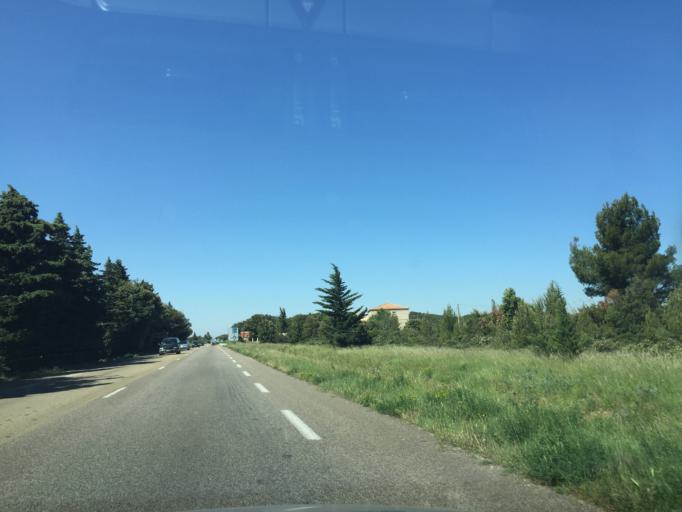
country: FR
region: Languedoc-Roussillon
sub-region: Departement du Gard
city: Saze
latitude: 43.9521
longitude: 4.6418
